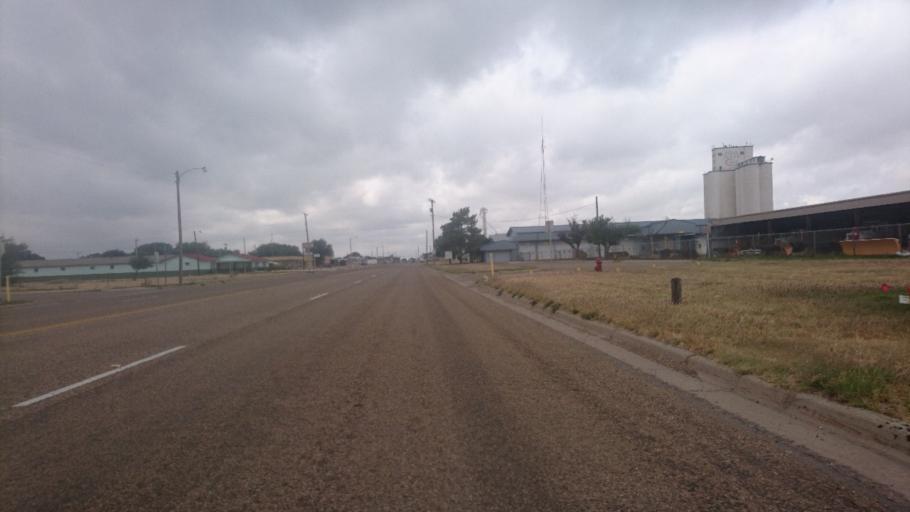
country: US
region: Texas
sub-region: Oldham County
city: Vega
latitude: 35.2430
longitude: -102.4229
